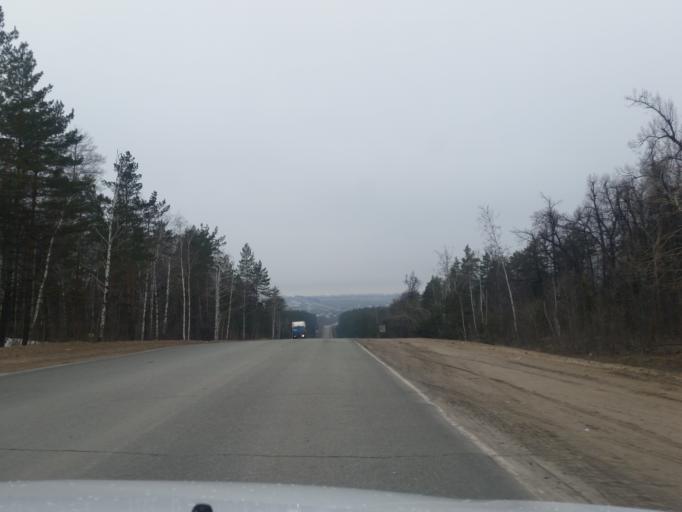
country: RU
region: Ulyanovsk
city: Mullovka
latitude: 54.2248
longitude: 49.4292
